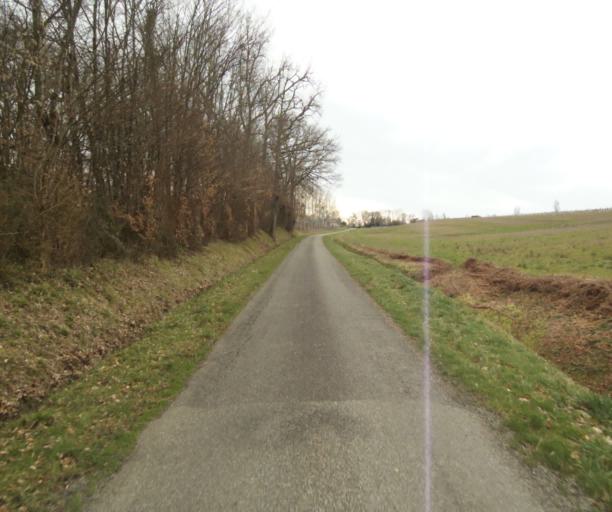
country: FR
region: Midi-Pyrenees
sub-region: Departement du Gers
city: Eauze
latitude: 43.9151
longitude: 0.0612
